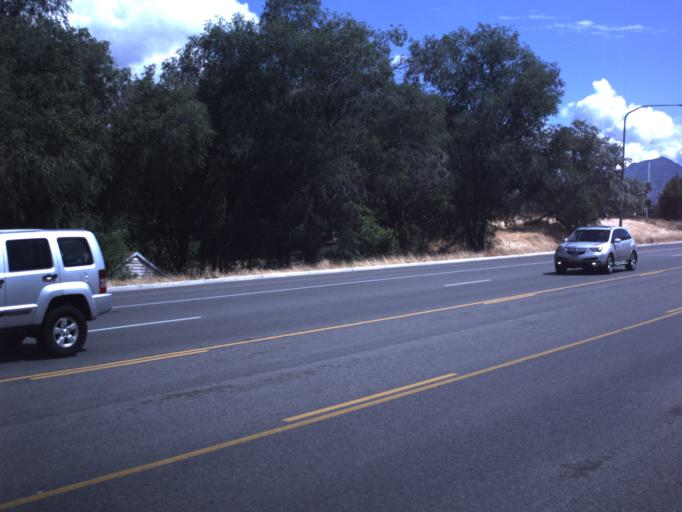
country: US
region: Utah
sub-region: Salt Lake County
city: Murray
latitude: 40.6531
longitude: -111.9134
